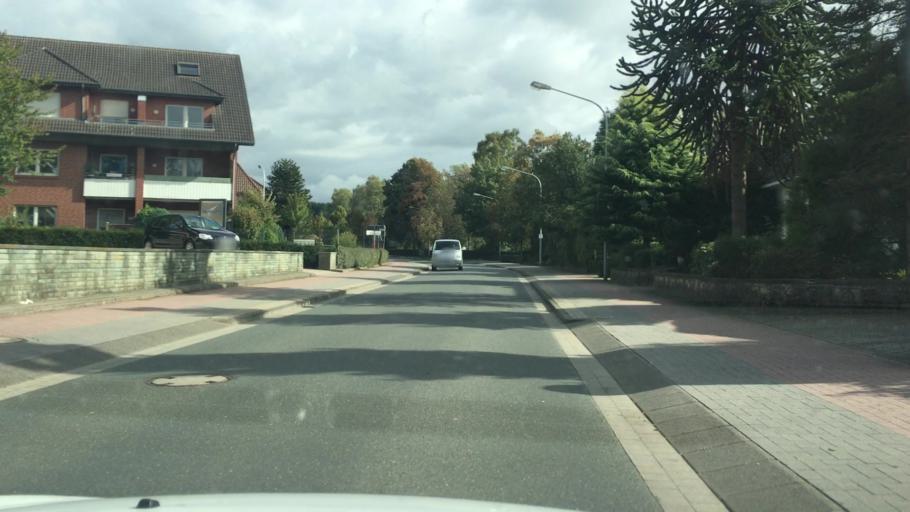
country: DE
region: Lower Saxony
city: Lohne
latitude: 52.6620
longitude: 8.2441
